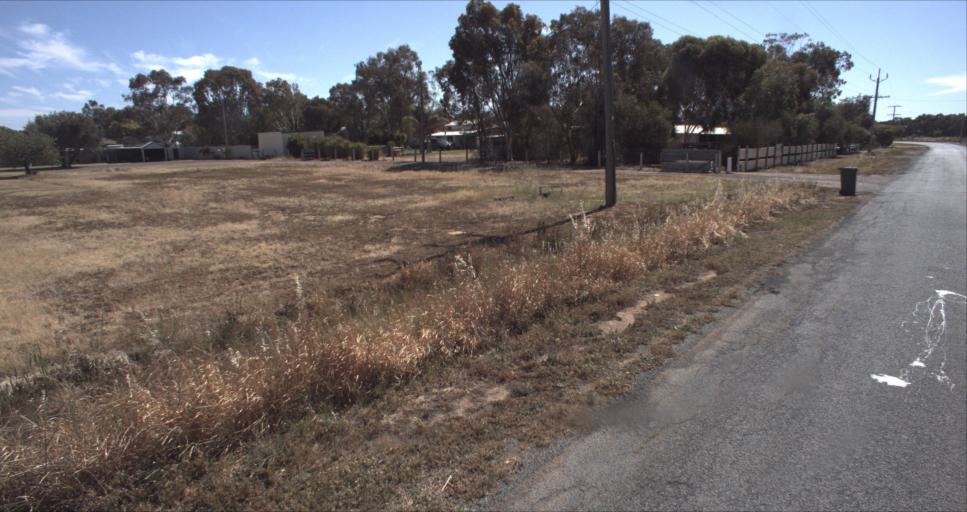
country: AU
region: New South Wales
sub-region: Leeton
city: Leeton
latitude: -34.5495
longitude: 146.3810
